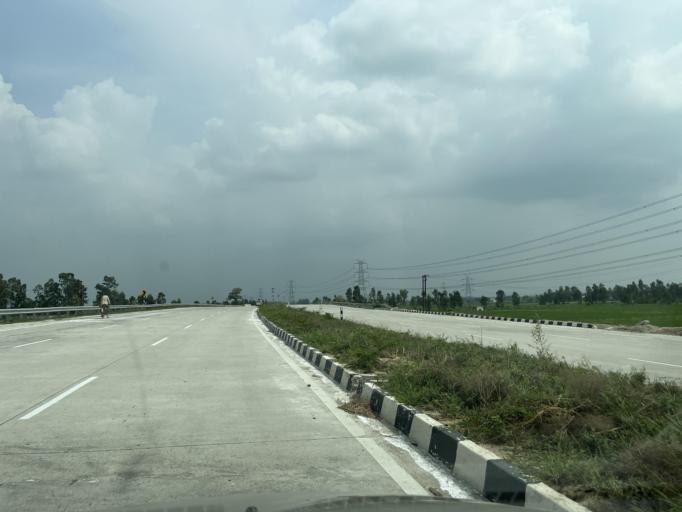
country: IN
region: Uttarakhand
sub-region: Udham Singh Nagar
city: Jaspur
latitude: 29.2897
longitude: 78.8522
